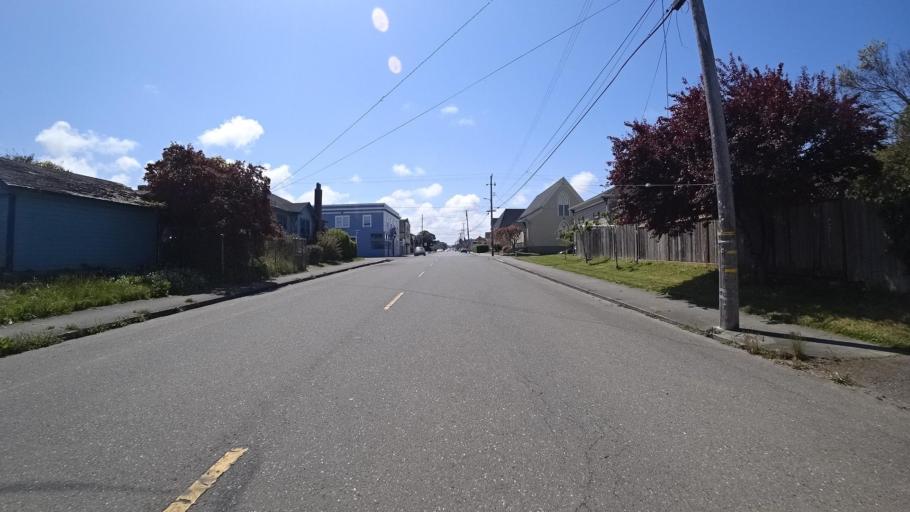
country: US
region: California
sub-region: Humboldt County
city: Eureka
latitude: 40.7954
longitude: -124.1719
